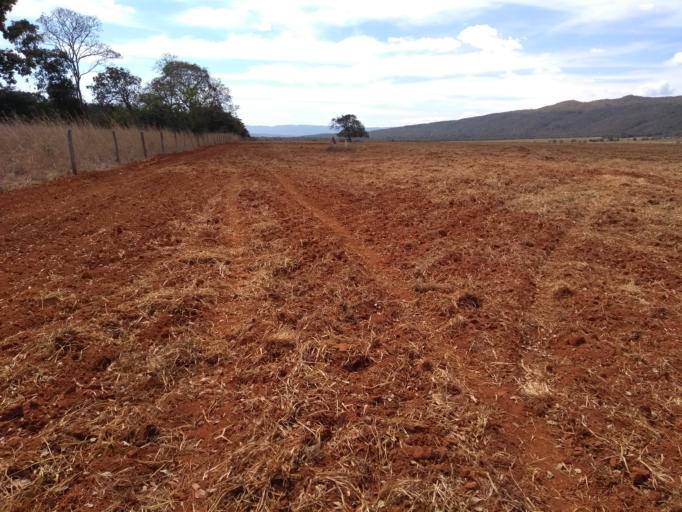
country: BR
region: Goias
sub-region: Formosa
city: Formosa
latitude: -15.3342
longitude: -47.3549
